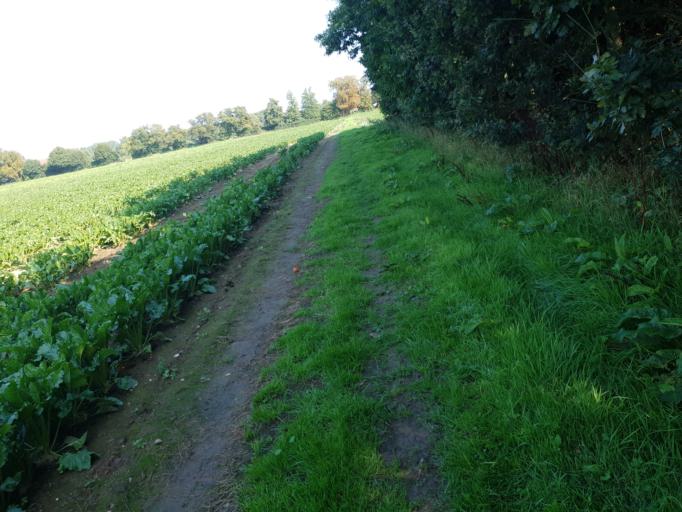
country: GB
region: England
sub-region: Suffolk
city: East Bergholt
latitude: 51.9498
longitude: 1.0090
